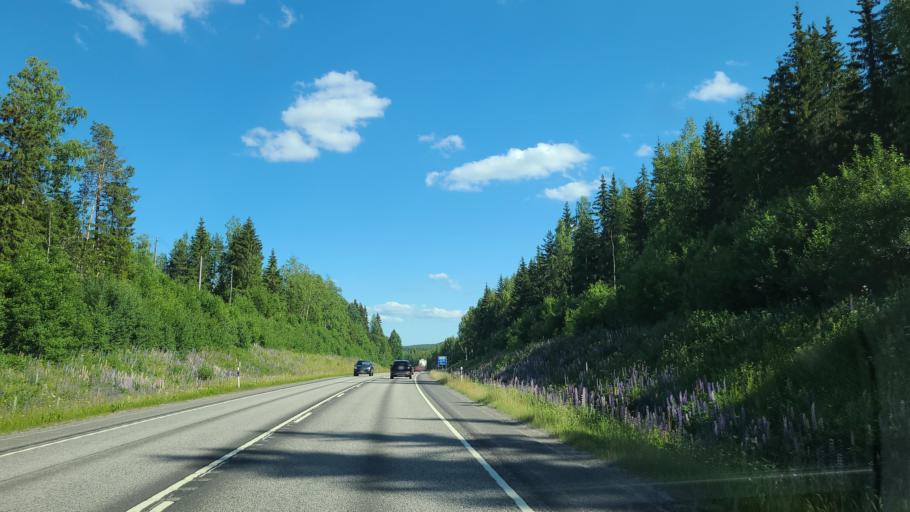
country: FI
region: Central Finland
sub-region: Jyvaeskylae
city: Jyvaeskylae
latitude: 62.2640
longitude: 25.5847
